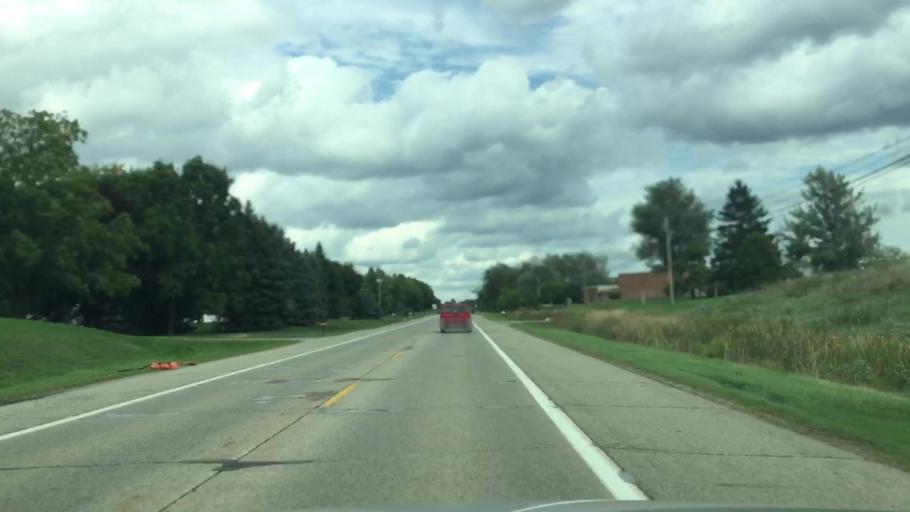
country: US
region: Michigan
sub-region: Shiawassee County
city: Owosso
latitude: 42.9631
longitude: -84.2004
